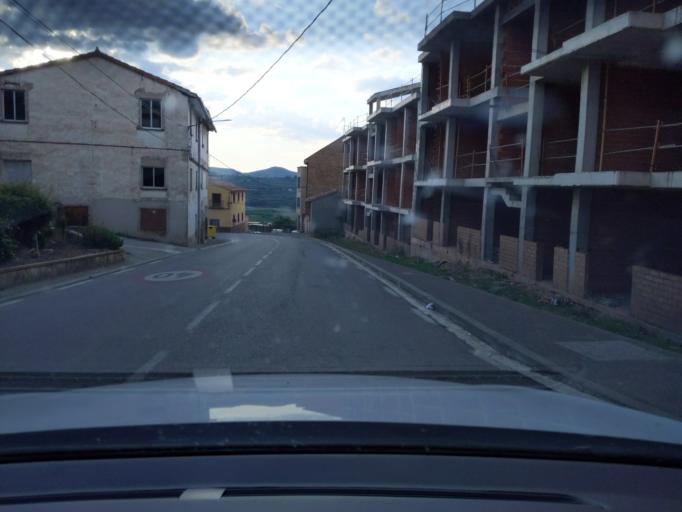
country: ES
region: La Rioja
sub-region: Provincia de La Rioja
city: Nalda
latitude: 42.3359
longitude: -2.4873
